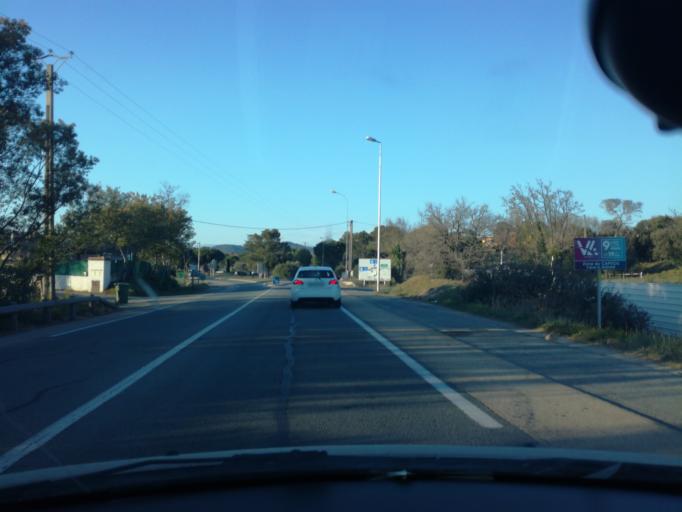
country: FR
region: Provence-Alpes-Cote d'Azur
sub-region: Departement du Var
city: Frejus
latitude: 43.4693
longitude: 6.7446
